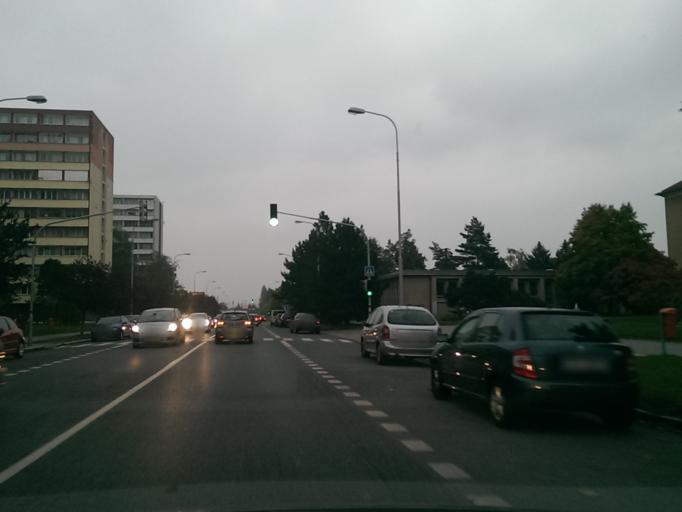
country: CZ
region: Central Bohemia
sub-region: Okres Mlada Boleslav
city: Mlada Boleslav
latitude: 50.4105
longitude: 14.9258
